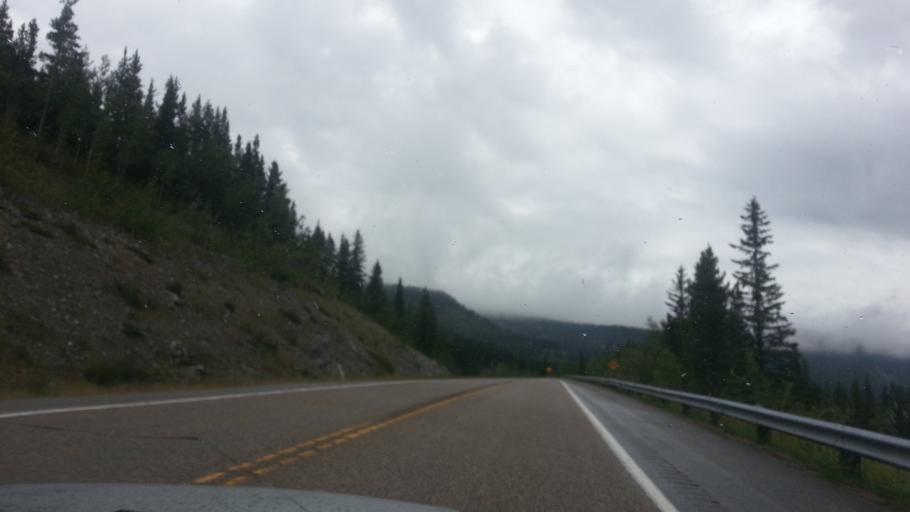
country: CA
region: Alberta
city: Cochrane
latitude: 50.8588
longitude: -114.7960
